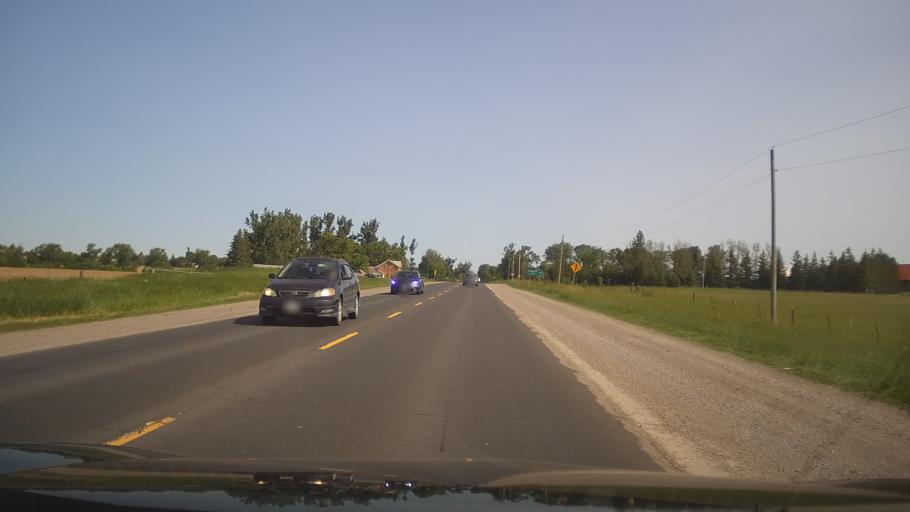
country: CA
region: Ontario
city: Omemee
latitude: 44.3292
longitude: -78.6867
